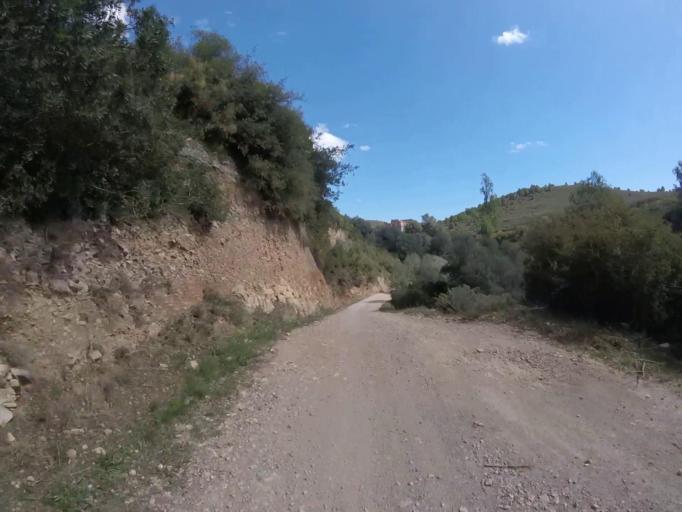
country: ES
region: Valencia
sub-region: Provincia de Castello
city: Santa Magdalena de Pulpis
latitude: 40.3255
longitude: 0.3366
